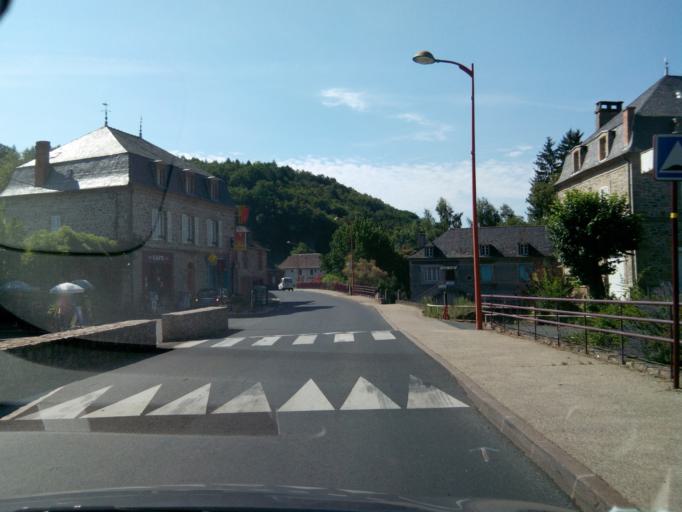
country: FR
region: Limousin
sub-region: Departement de la Correze
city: Beynat
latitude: 45.1298
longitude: 1.6592
